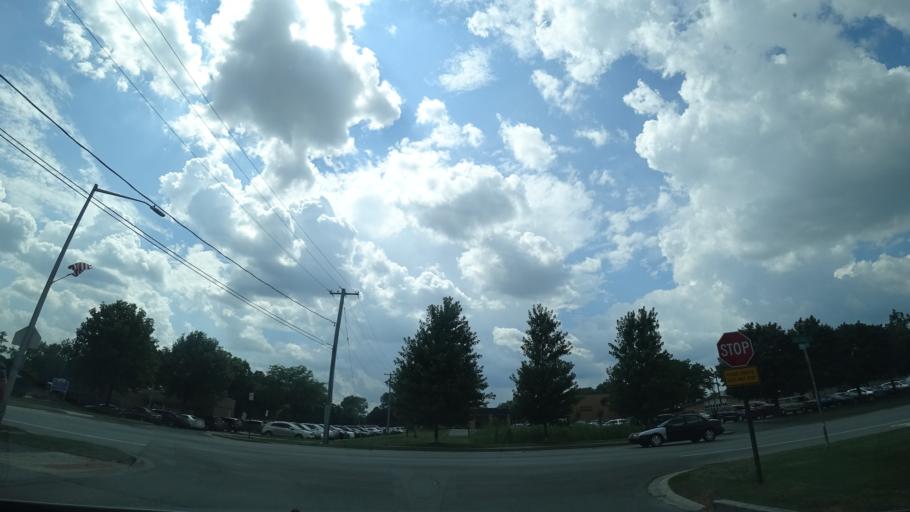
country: US
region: Illinois
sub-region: Cook County
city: Alsip
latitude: 41.6756
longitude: -87.7292
